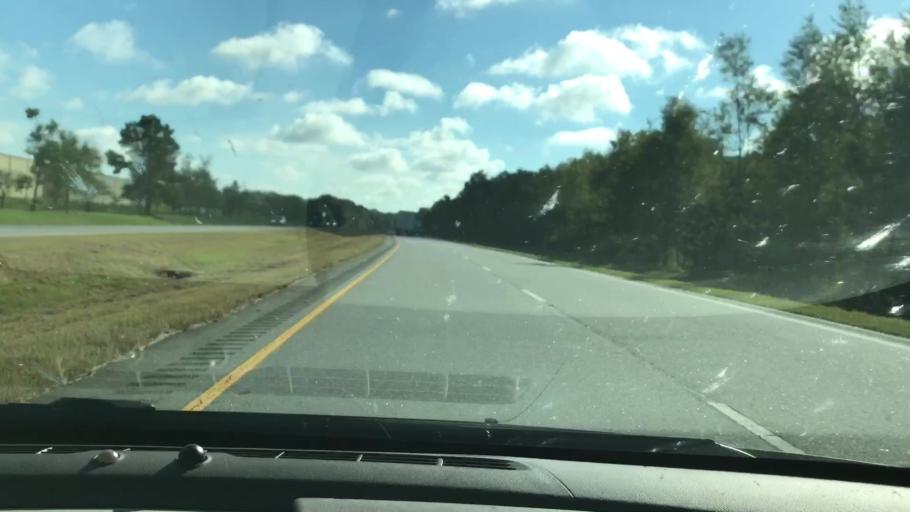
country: US
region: Georgia
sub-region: Dougherty County
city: Albany
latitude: 31.5803
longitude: -84.0699
